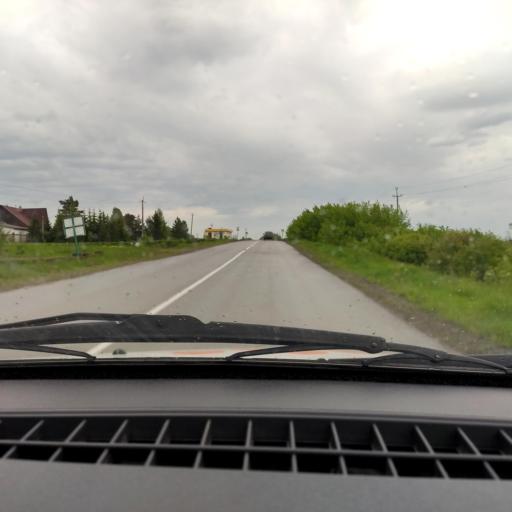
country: RU
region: Bashkortostan
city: Kudeyevskiy
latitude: 54.8264
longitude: 56.7932
